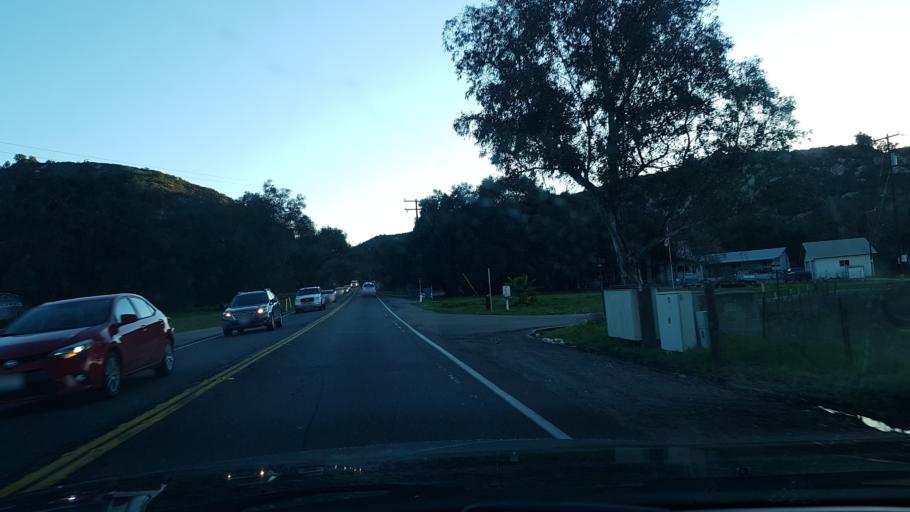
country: US
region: California
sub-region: San Diego County
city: Lakeside
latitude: 32.9302
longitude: -116.8717
